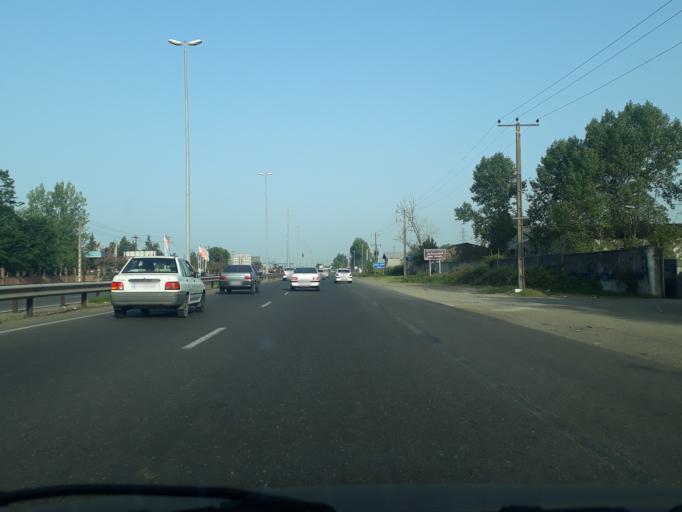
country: IR
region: Gilan
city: Bandar-e Anzali
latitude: 37.4603
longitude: 49.5764
